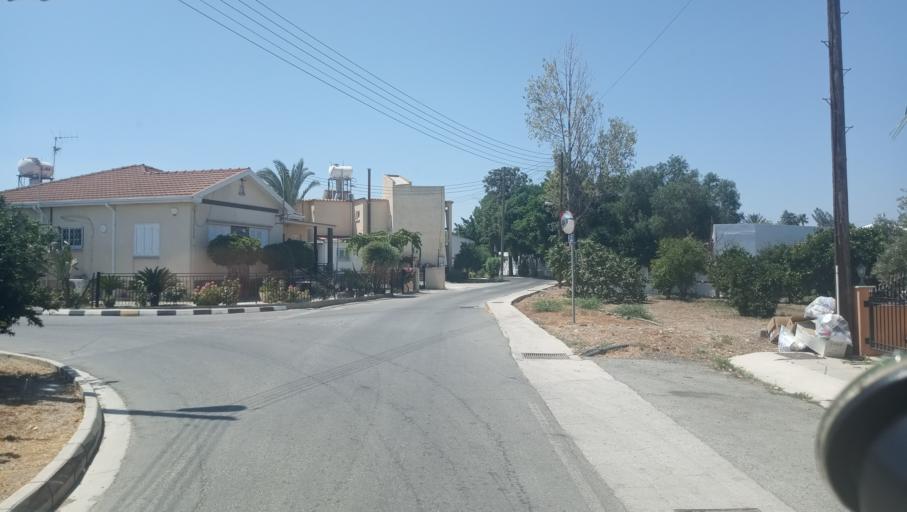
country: CY
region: Lefkosia
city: Psimolofou
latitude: 35.0622
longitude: 33.2607
